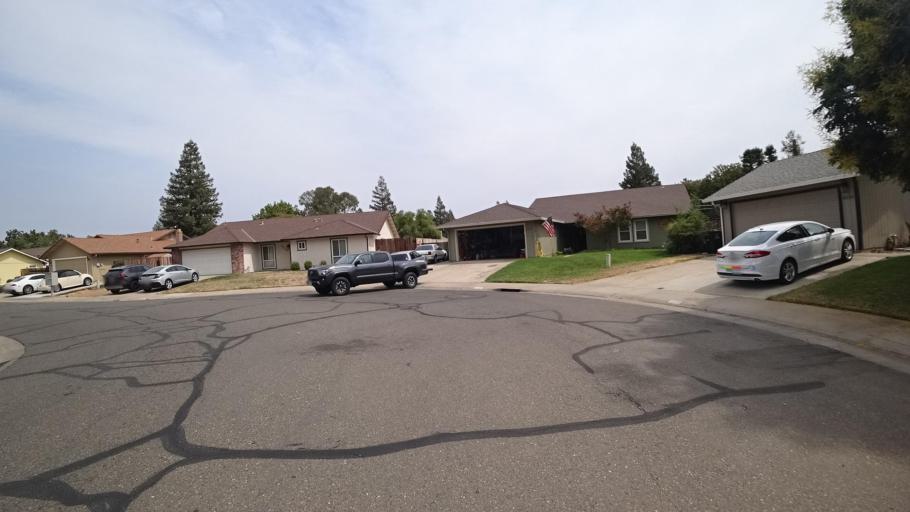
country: US
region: California
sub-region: Sacramento County
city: Elk Grove
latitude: 38.4150
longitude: -121.3879
